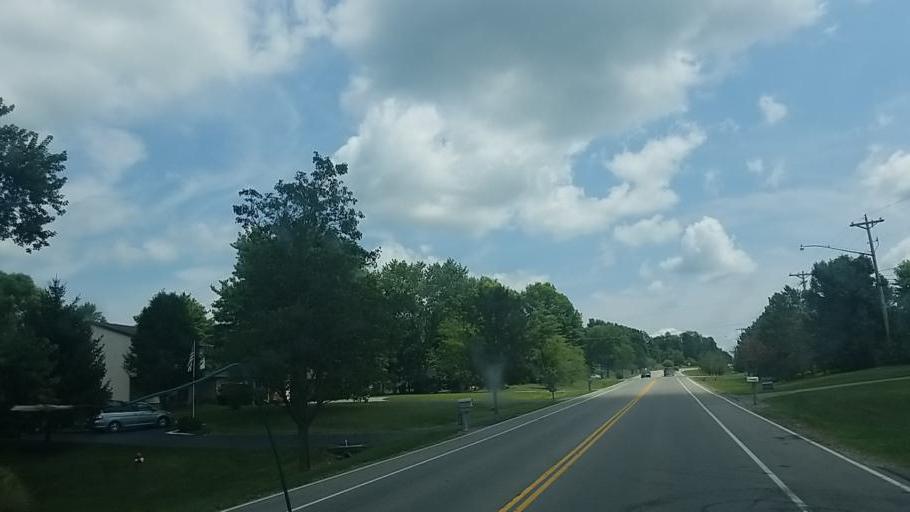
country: US
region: Ohio
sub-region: Fairfield County
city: Pickerington
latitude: 39.8836
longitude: -82.7442
